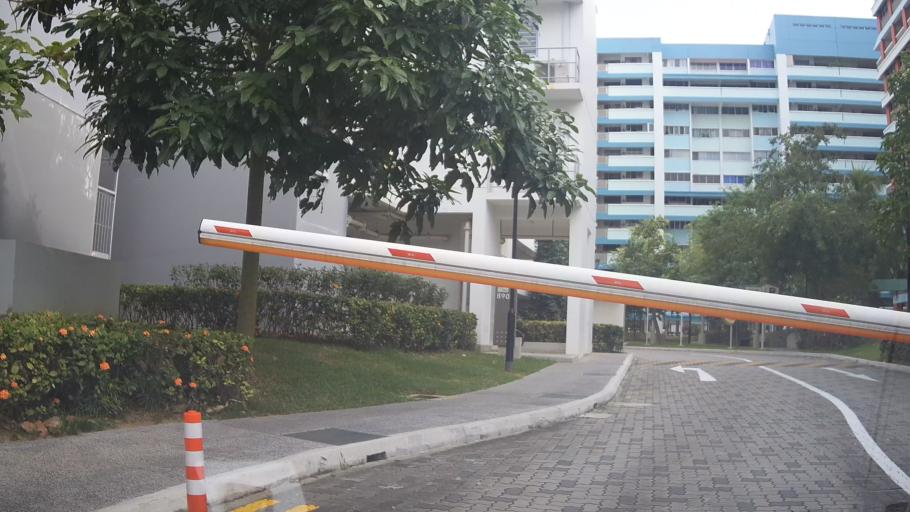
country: SG
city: Singapore
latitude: 1.3465
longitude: 103.9344
